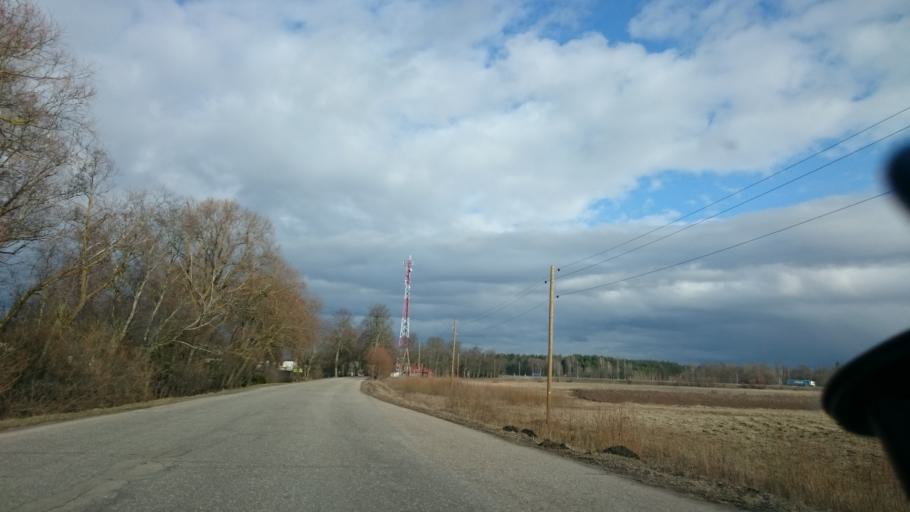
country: LV
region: Adazi
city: Adazi
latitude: 57.1173
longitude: 24.3148
